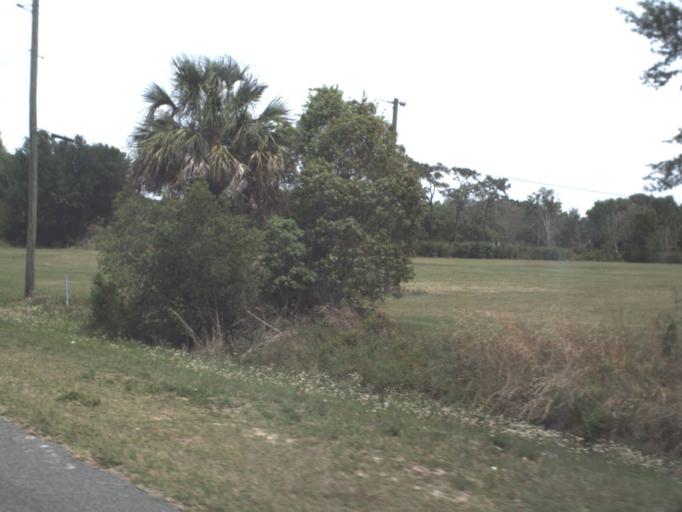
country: US
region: Florida
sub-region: Lake County
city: Mount Dora
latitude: 28.8422
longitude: -81.6337
